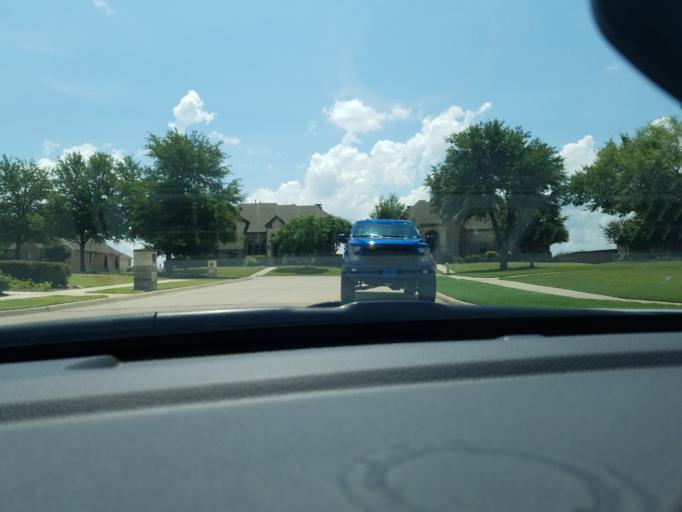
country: US
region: Texas
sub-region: Dallas County
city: Sunnyvale
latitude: 32.8107
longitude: -96.5770
